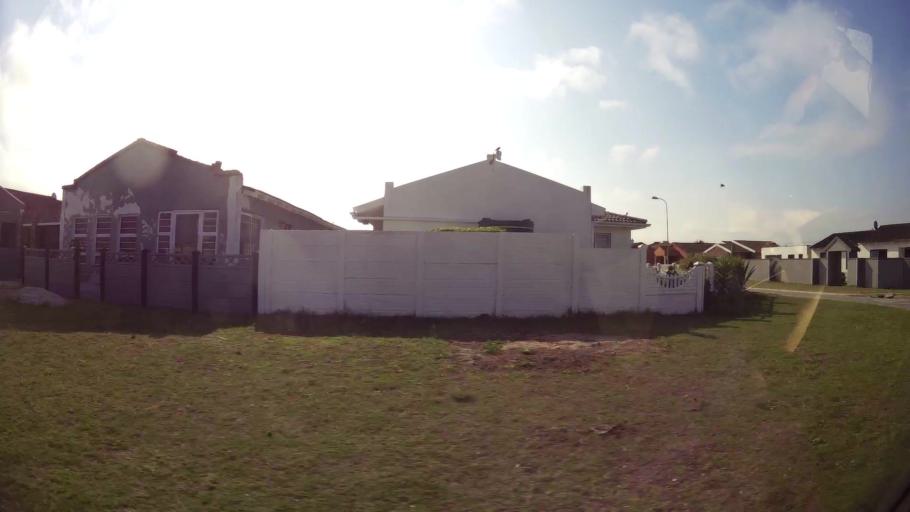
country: ZA
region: Eastern Cape
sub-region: Nelson Mandela Bay Metropolitan Municipality
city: Port Elizabeth
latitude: -33.9198
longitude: 25.5332
